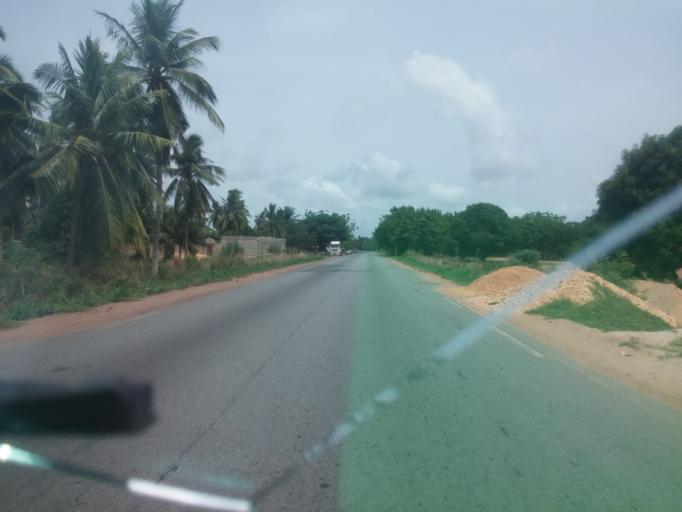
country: TG
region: Maritime
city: Aneho
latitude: 6.2220
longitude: 1.5143
